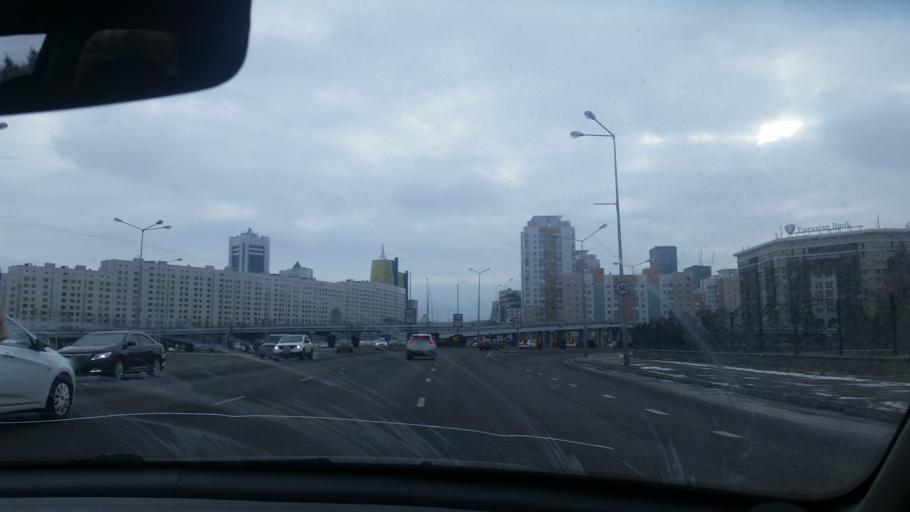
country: KZ
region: Astana Qalasy
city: Astana
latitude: 51.1344
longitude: 71.4412
